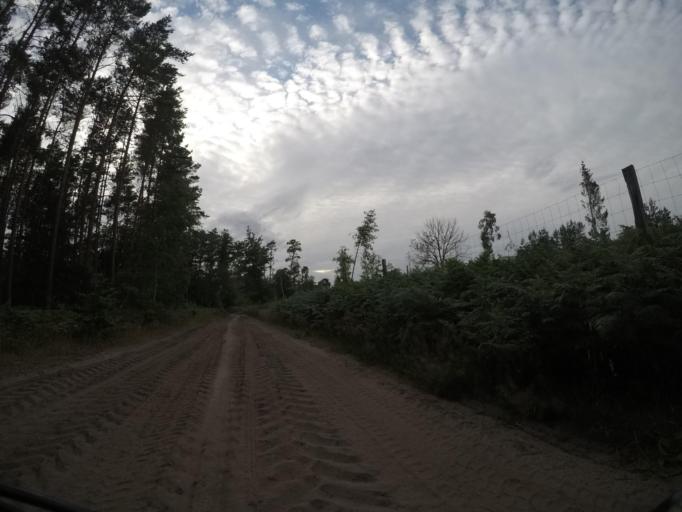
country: DE
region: Mecklenburg-Vorpommern
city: Lubtheen
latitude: 53.2486
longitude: 11.0339
